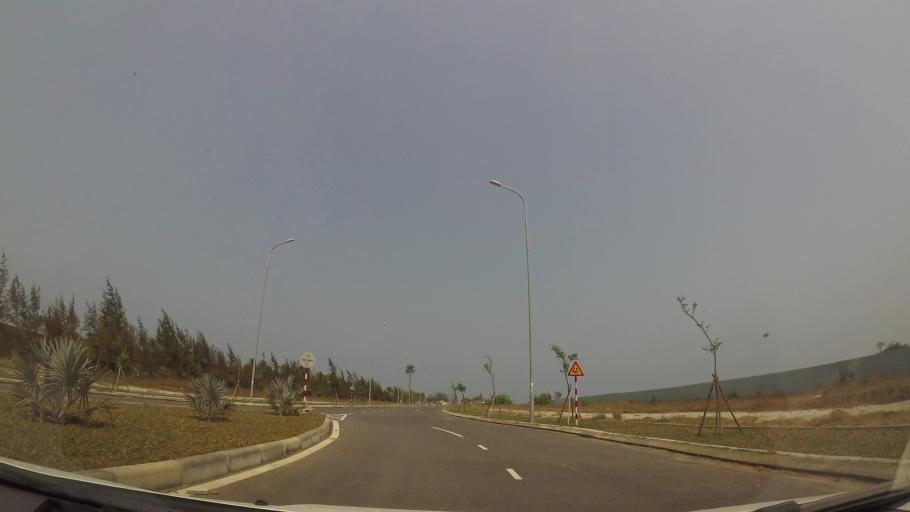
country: VN
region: Da Nang
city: Ngu Hanh Son
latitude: 15.9869
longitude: 108.2736
